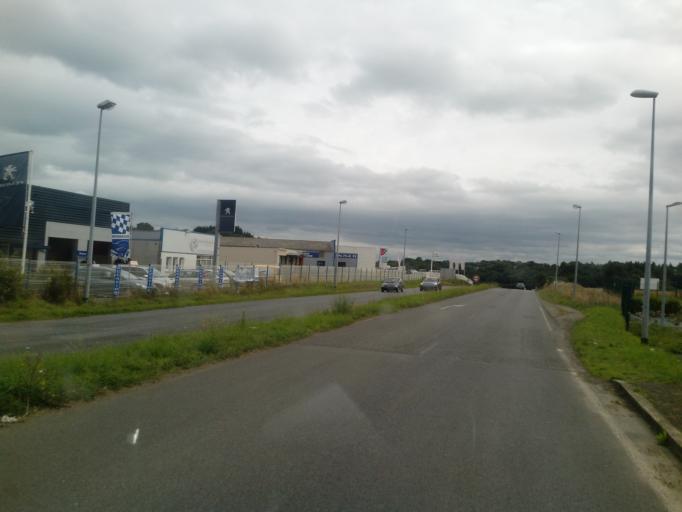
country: FR
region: Brittany
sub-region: Departement des Cotes-d'Armor
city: Saint-Quay-Portrieux
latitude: 48.6425
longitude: -2.8366
